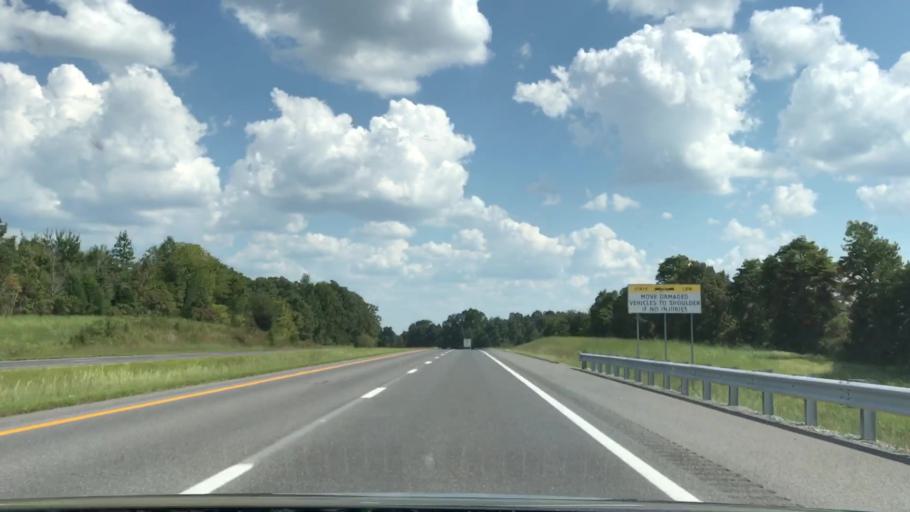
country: US
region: Kentucky
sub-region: Lyon County
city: Eddyville
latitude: 37.1072
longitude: -87.9918
